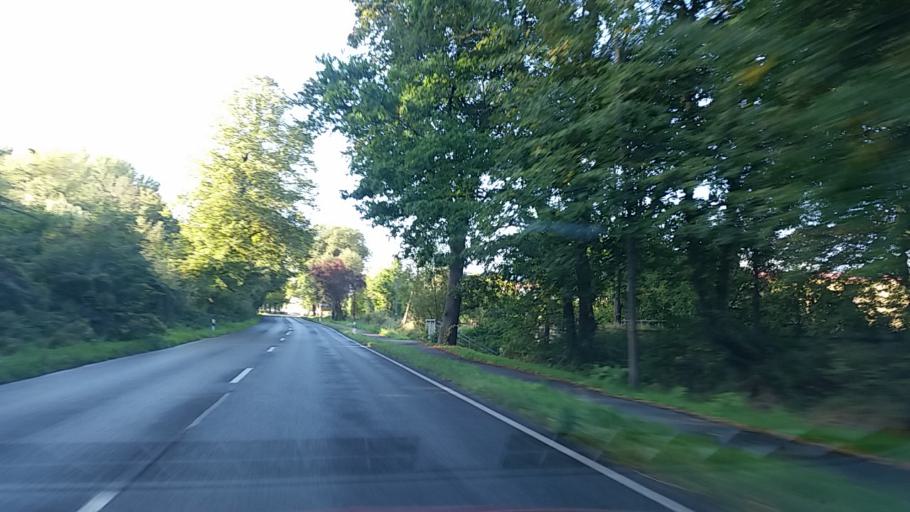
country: DE
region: Lower Saxony
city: Vordorf
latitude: 52.3266
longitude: 10.5230
